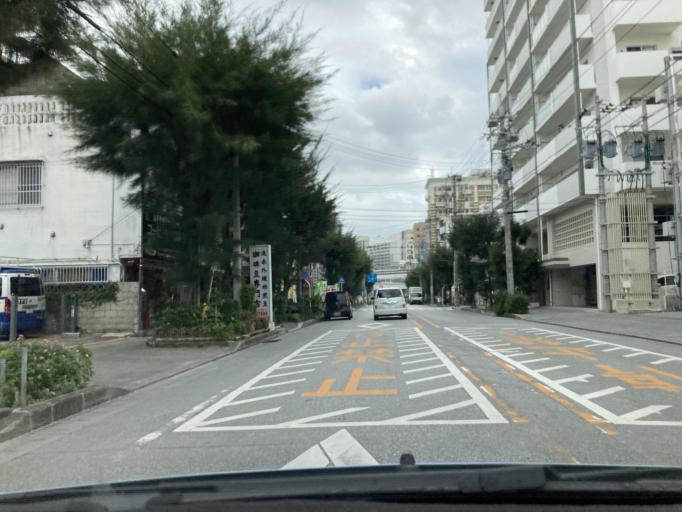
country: JP
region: Okinawa
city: Naha-shi
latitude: 26.2143
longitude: 127.6739
